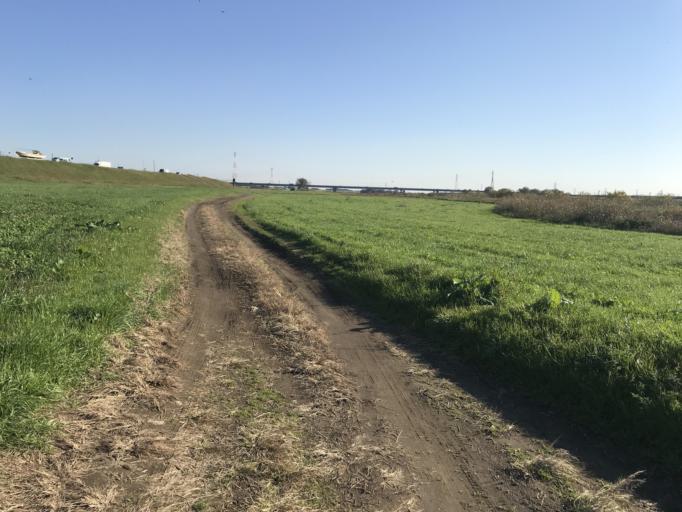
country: JP
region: Ibaraki
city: Sakai
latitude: 36.1069
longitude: 139.7862
